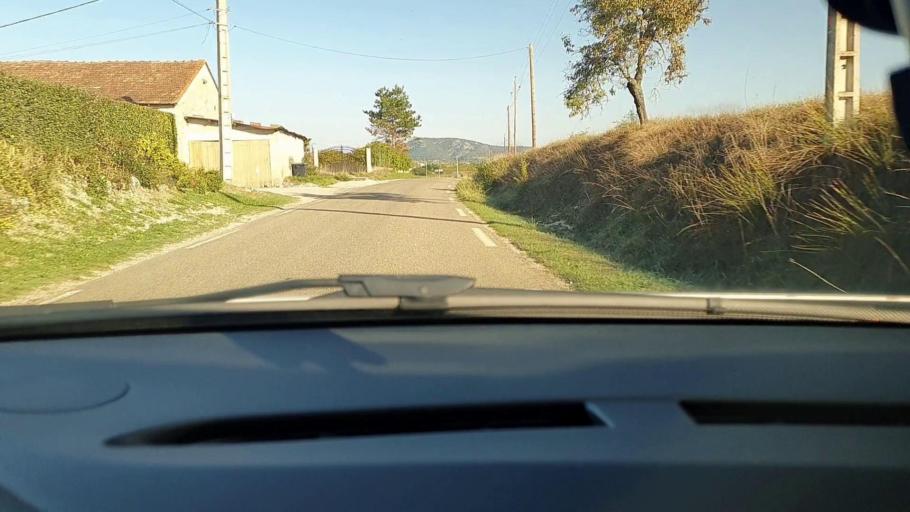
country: FR
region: Languedoc-Roussillon
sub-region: Departement du Gard
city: Saint-Ambroix
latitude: 44.2692
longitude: 4.2761
